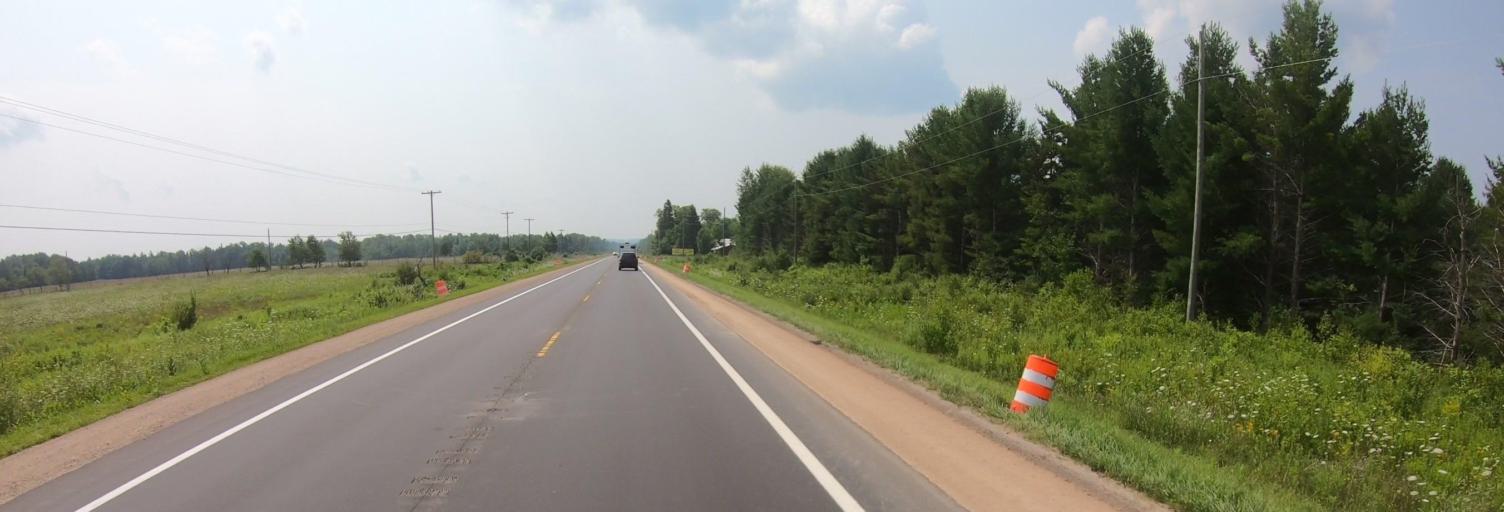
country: US
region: Michigan
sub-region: Luce County
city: Newberry
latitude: 46.4021
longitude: -85.5100
